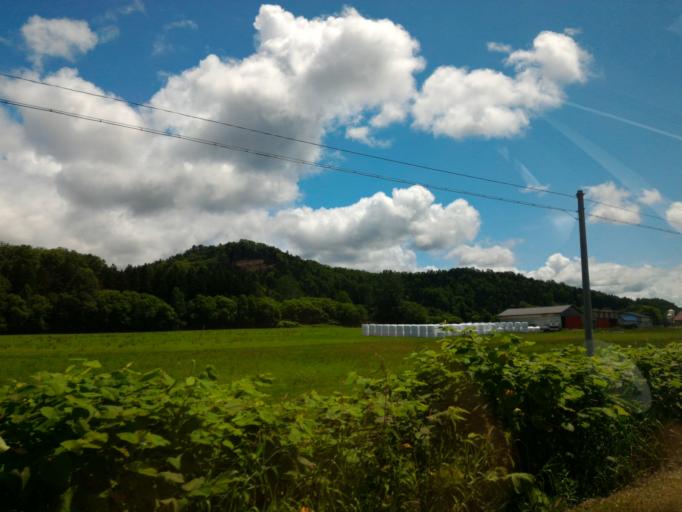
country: JP
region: Hokkaido
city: Nayoro
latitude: 44.5971
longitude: 142.3105
